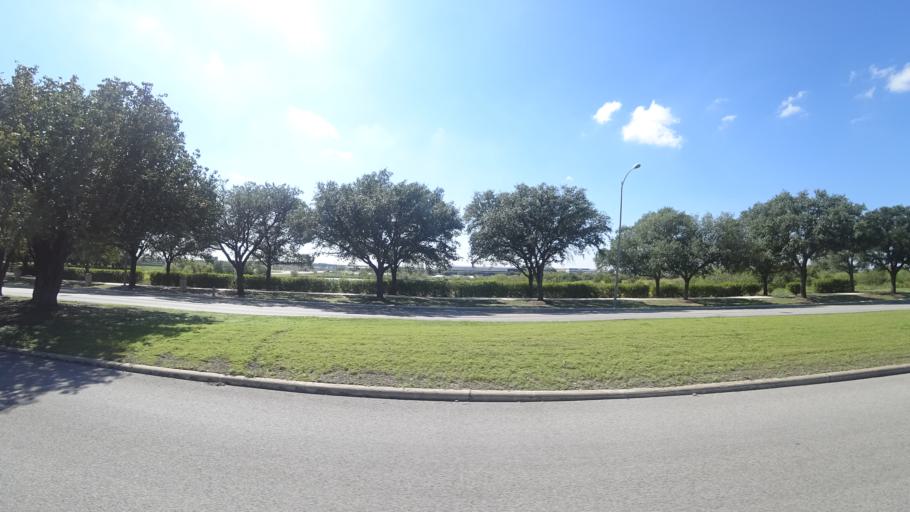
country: US
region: Texas
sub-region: Travis County
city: Manor
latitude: 30.3364
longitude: -97.6080
